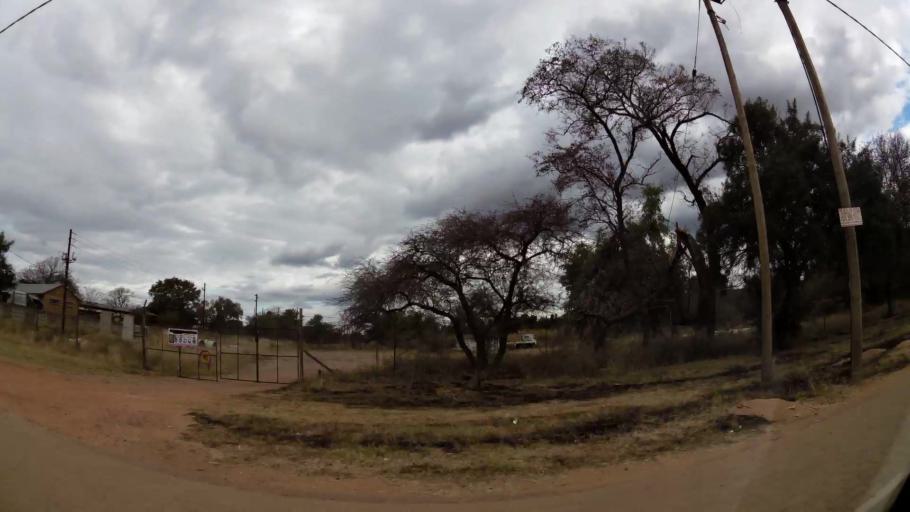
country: ZA
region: Limpopo
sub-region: Waterberg District Municipality
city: Modimolle
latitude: -24.7009
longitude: 28.4152
